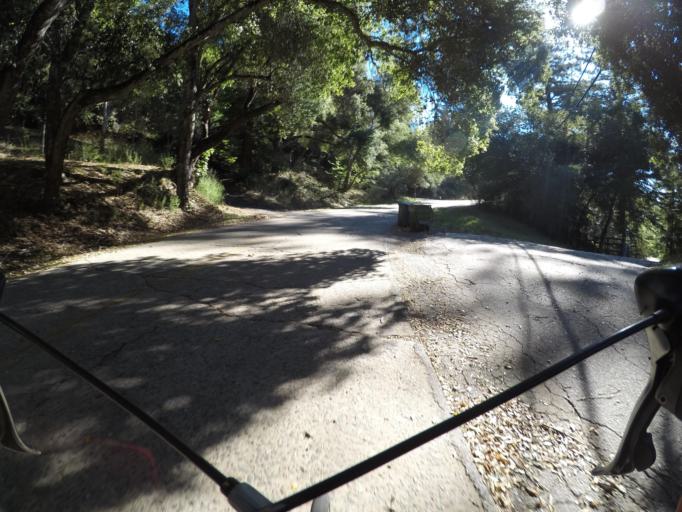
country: US
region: California
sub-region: Santa Clara County
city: Lexington Hills
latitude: 37.1244
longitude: -121.9825
